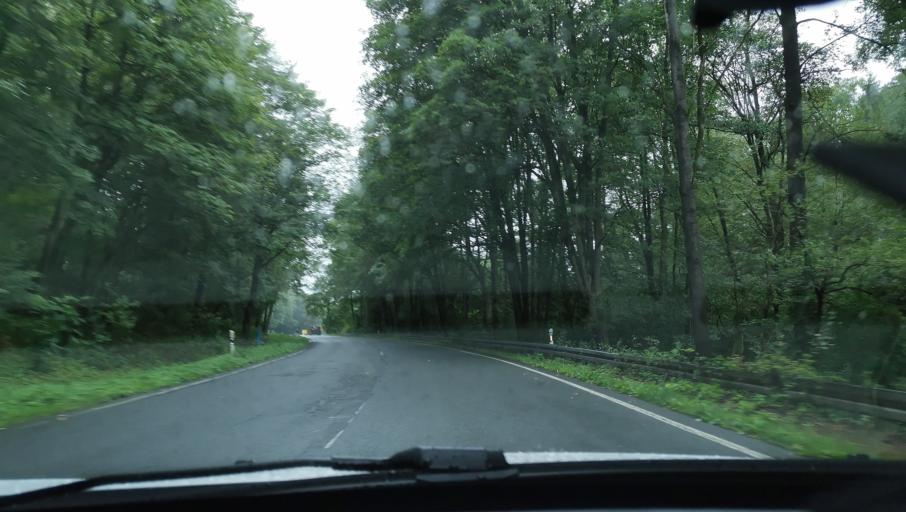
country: DE
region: North Rhine-Westphalia
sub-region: Regierungsbezirk Arnsberg
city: Breckerfeld
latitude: 51.2482
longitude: 7.4873
